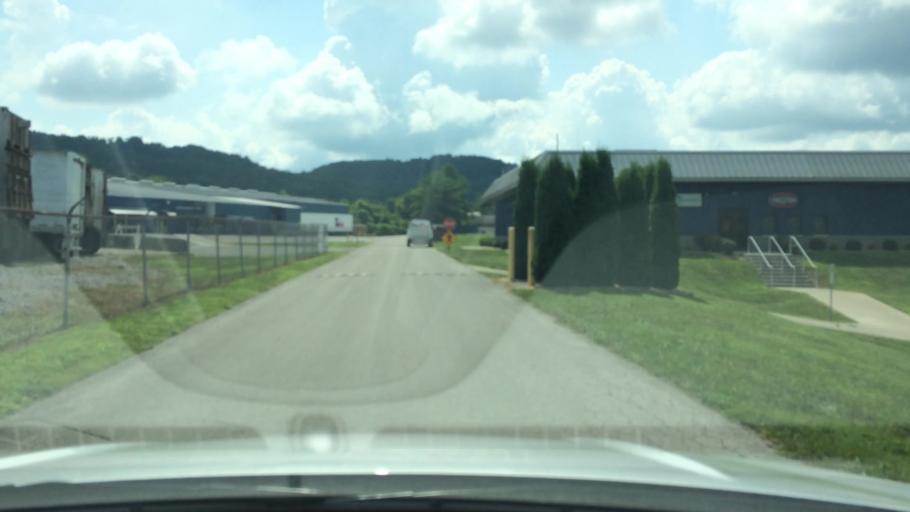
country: US
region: Kentucky
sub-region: Pulaski County
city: Somerset
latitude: 36.9703
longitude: -84.5860
